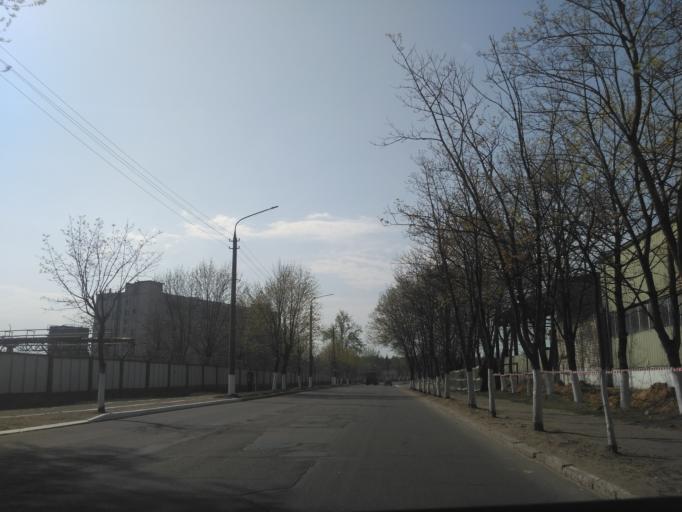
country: BY
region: Minsk
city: Horad Barysaw
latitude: 54.2021
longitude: 28.5162
